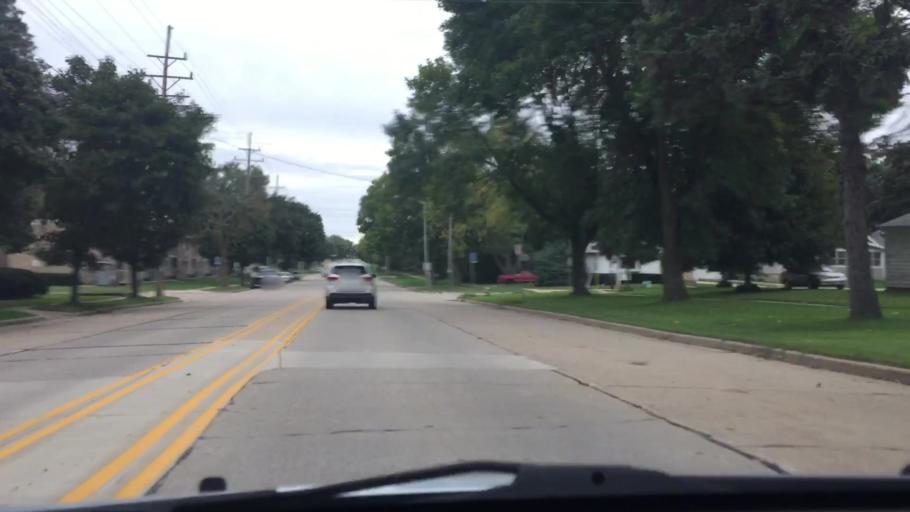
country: US
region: Wisconsin
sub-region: Waukesha County
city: Waukesha
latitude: 43.0200
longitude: -88.2393
